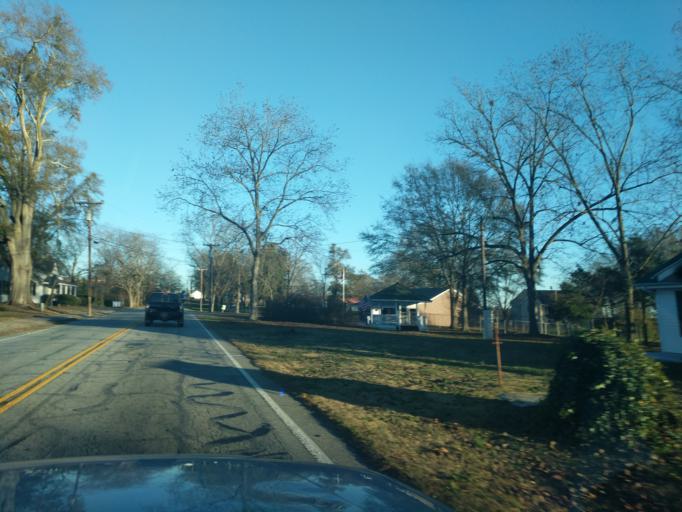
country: US
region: South Carolina
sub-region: Oconee County
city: Utica
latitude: 34.5643
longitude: -82.9021
